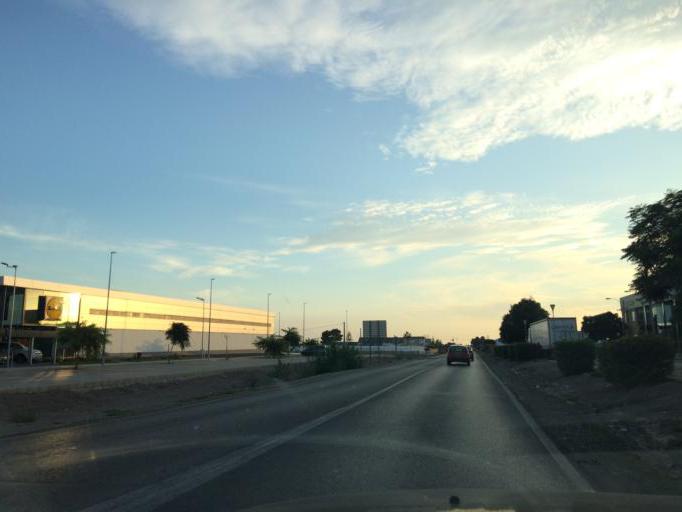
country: ES
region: Andalusia
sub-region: Provincia de Almeria
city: Nijar
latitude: 36.9270
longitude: -2.1447
